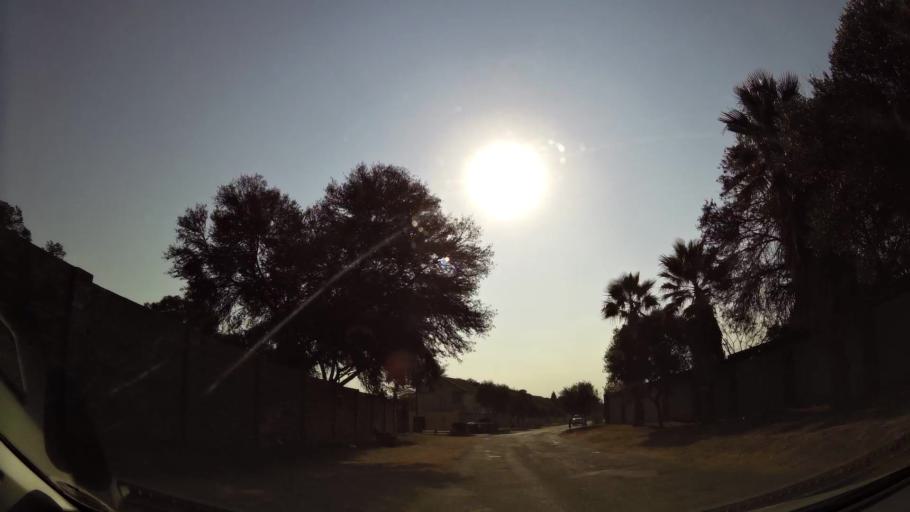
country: ZA
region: Gauteng
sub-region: City of Tshwane Metropolitan Municipality
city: Pretoria
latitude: -25.7613
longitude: 28.3302
